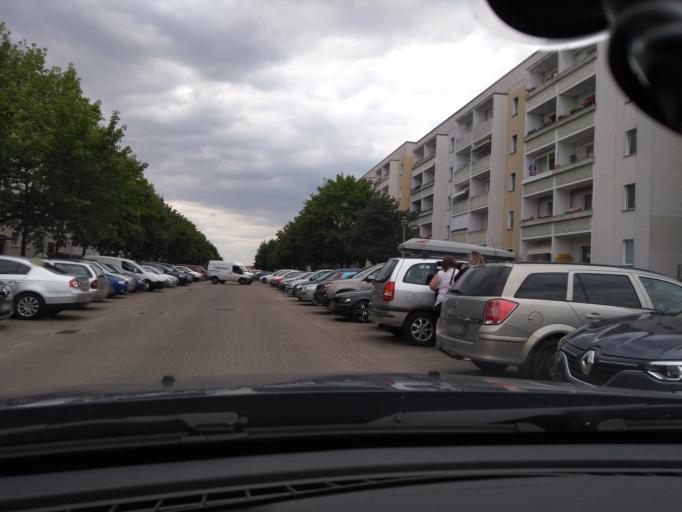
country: DE
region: Brandenburg
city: Falkensee
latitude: 52.5594
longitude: 13.0750
